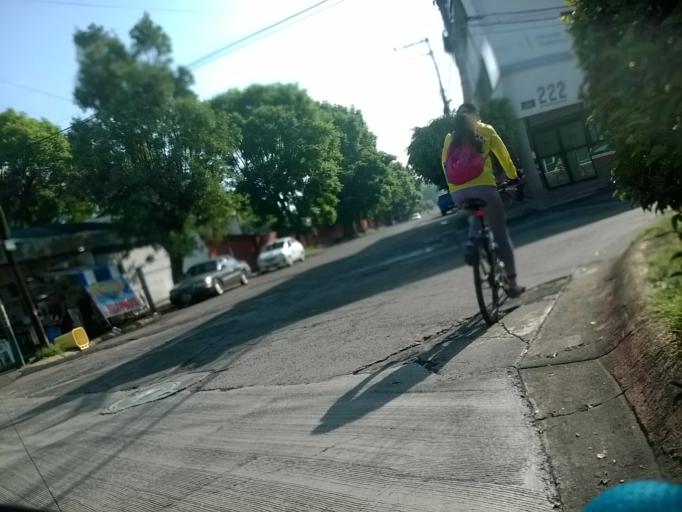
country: MX
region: Michoacan
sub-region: Morelia
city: Morelos
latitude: 19.6787
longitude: -101.2256
